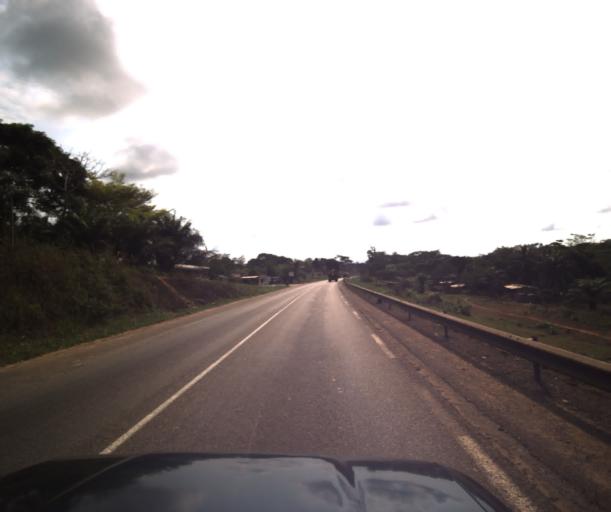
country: CM
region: Littoral
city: Edea
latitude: 3.9502
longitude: 10.0266
